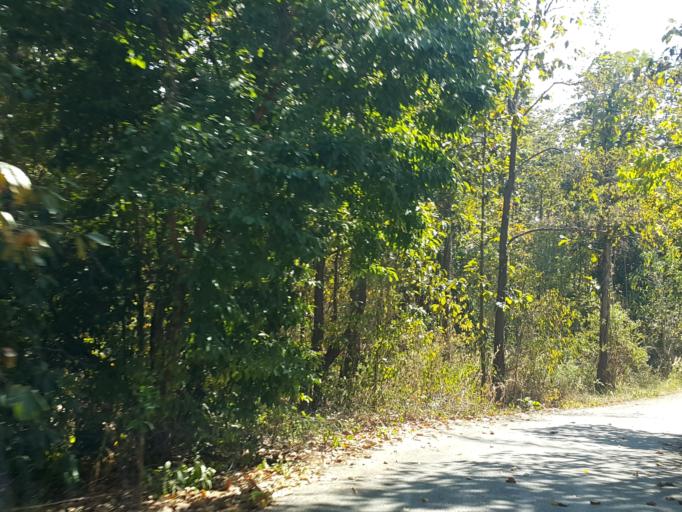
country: TH
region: Chiang Mai
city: Mae Taeng
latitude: 19.0330
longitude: 98.9916
